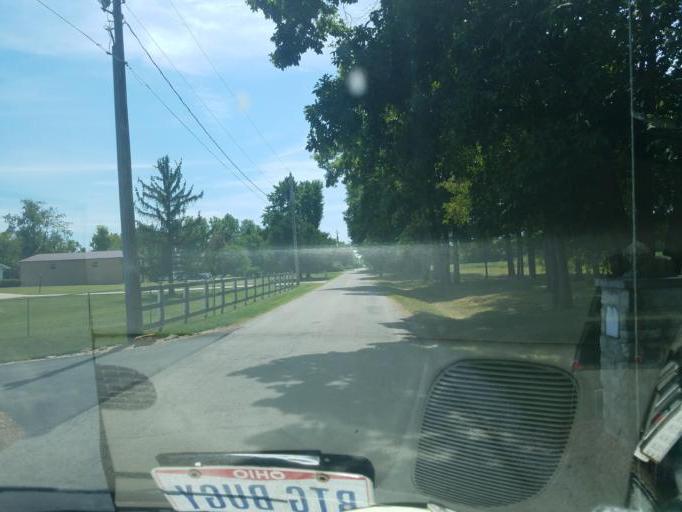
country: US
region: Ohio
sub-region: Franklin County
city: Lake Darby
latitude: 39.8430
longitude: -83.2132
